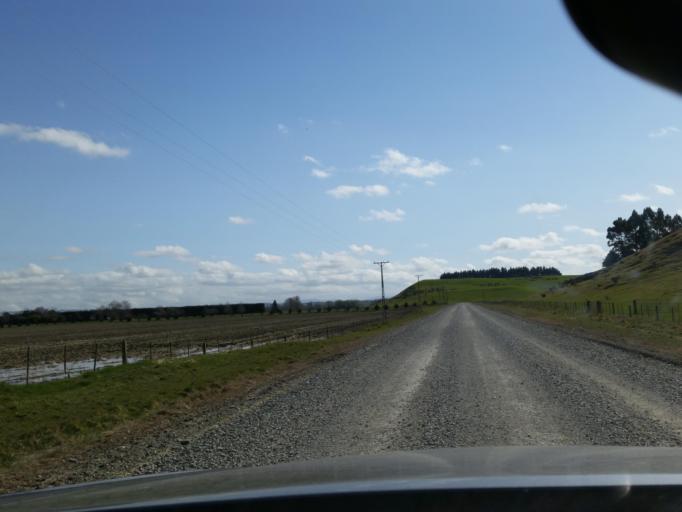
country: NZ
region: Southland
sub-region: Gore District
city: Gore
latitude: -45.8021
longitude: 168.6693
